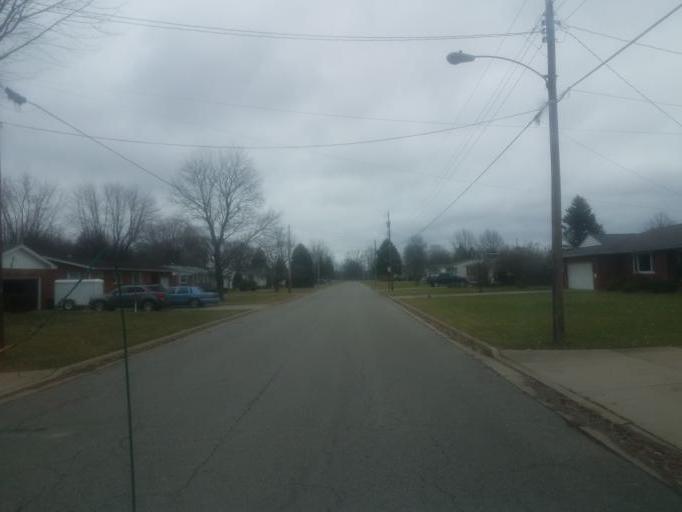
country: US
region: Ohio
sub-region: Crawford County
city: Crestline
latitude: 40.7743
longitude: -82.7362
